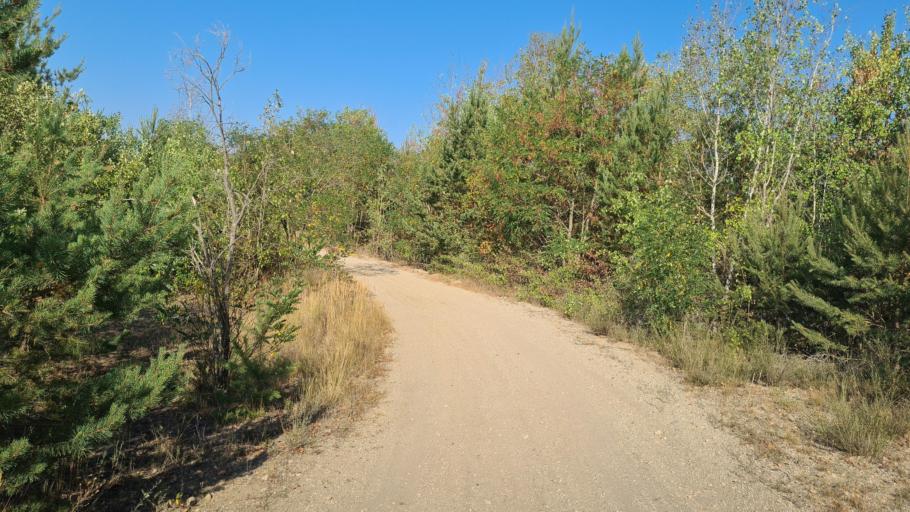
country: DE
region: Brandenburg
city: Sallgast
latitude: 51.5662
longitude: 13.8211
